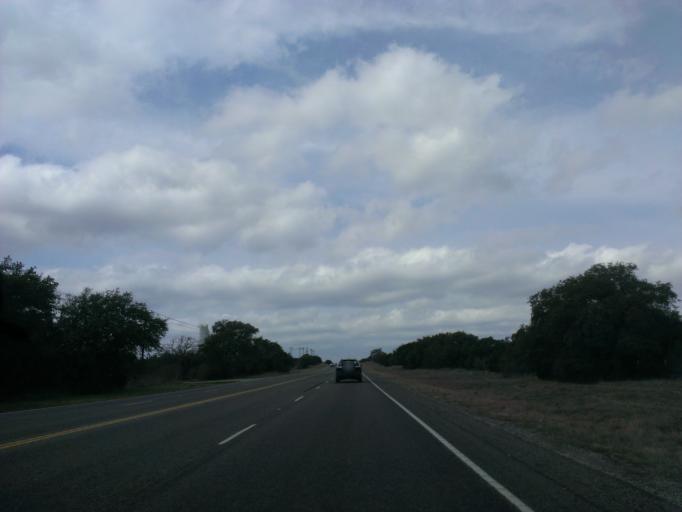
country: US
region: Texas
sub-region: Burnet County
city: Marble Falls
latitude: 30.4852
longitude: -98.2064
